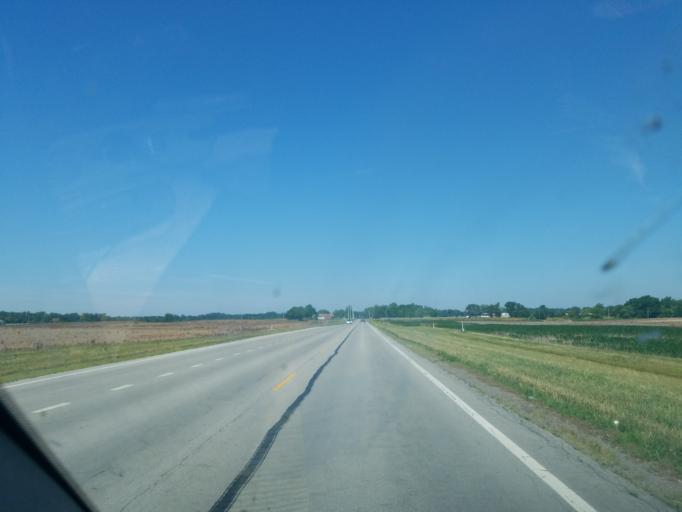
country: US
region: Ohio
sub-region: Logan County
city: Russells Point
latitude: 40.4650
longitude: -83.8160
